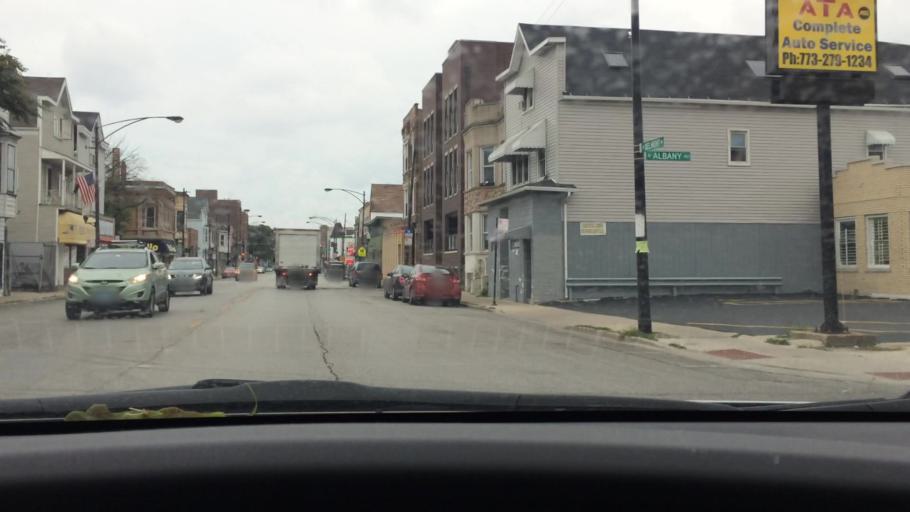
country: US
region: Illinois
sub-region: Cook County
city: Lincolnwood
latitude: 41.9393
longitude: -87.7048
